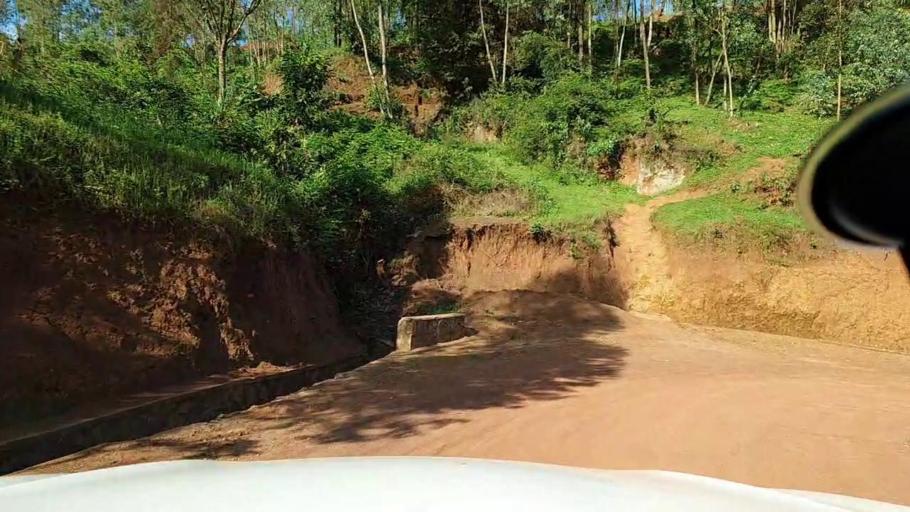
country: RW
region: Kigali
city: Kigali
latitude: -1.8386
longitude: 29.8546
